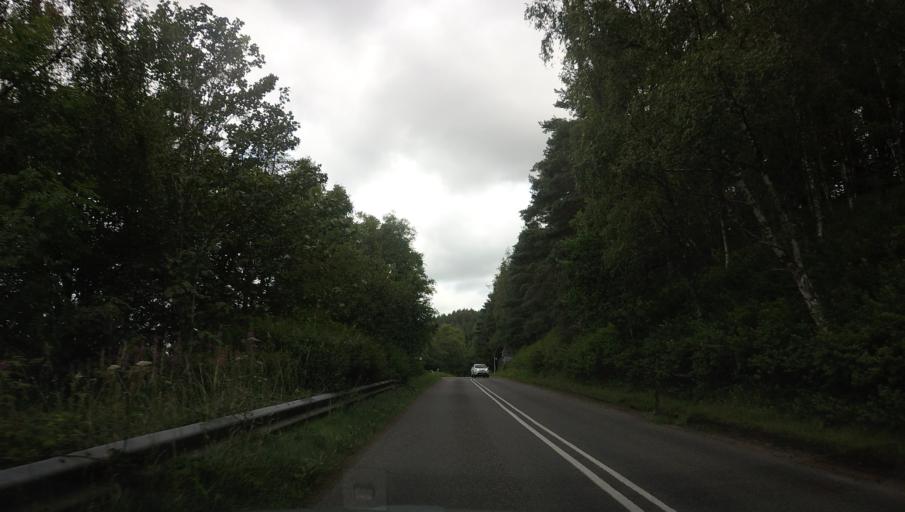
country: GB
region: Scotland
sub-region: Aberdeenshire
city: Torphins
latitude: 57.0648
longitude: -2.6475
